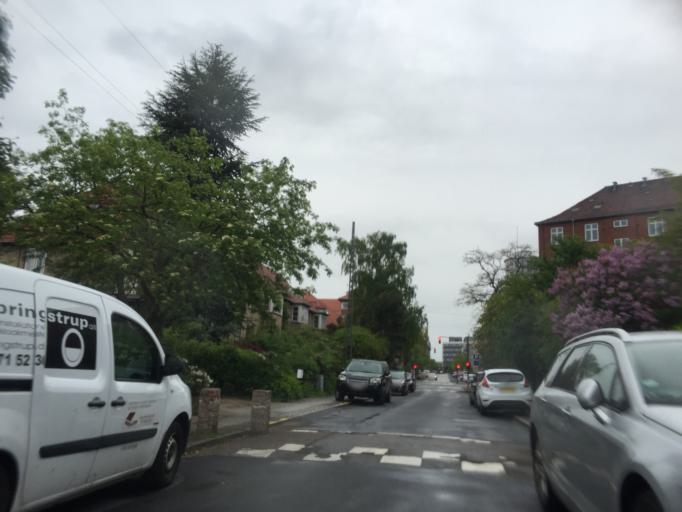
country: DK
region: Capital Region
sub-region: Kobenhavn
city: Vanlose
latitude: 55.6815
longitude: 12.5027
